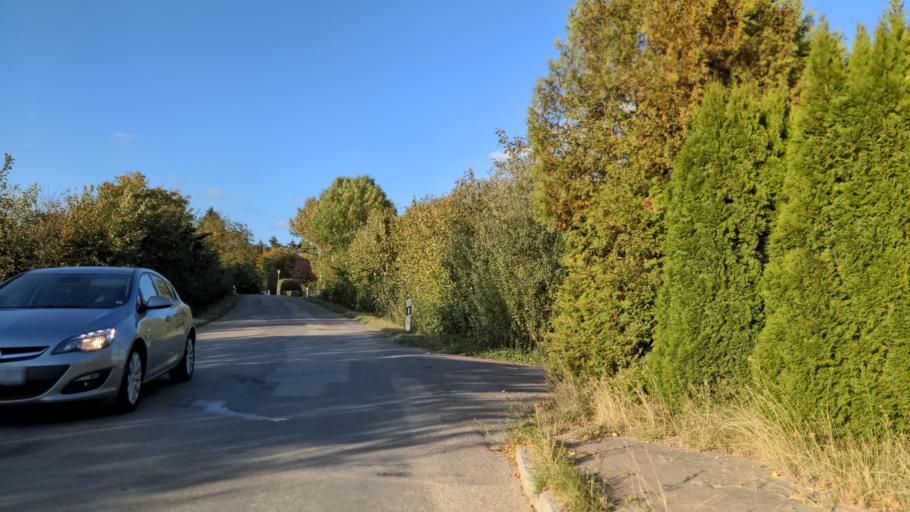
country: DE
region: Schleswig-Holstein
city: Strukdorf
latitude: 53.9531
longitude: 10.5252
